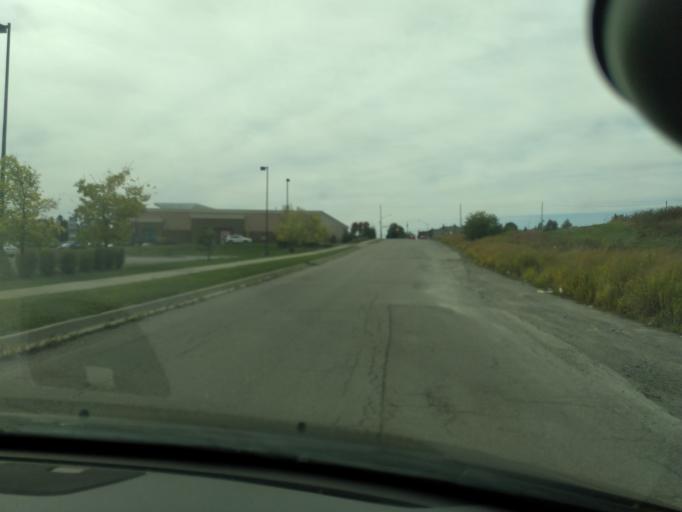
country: CA
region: Ontario
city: Newmarket
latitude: 44.0775
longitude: -79.4828
